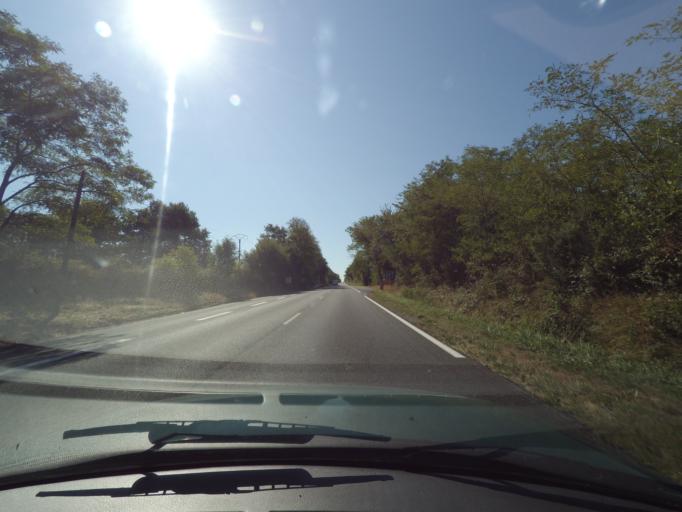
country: FR
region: Poitou-Charentes
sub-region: Departement de la Vienne
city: Saulge
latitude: 46.3441
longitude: 0.7956
